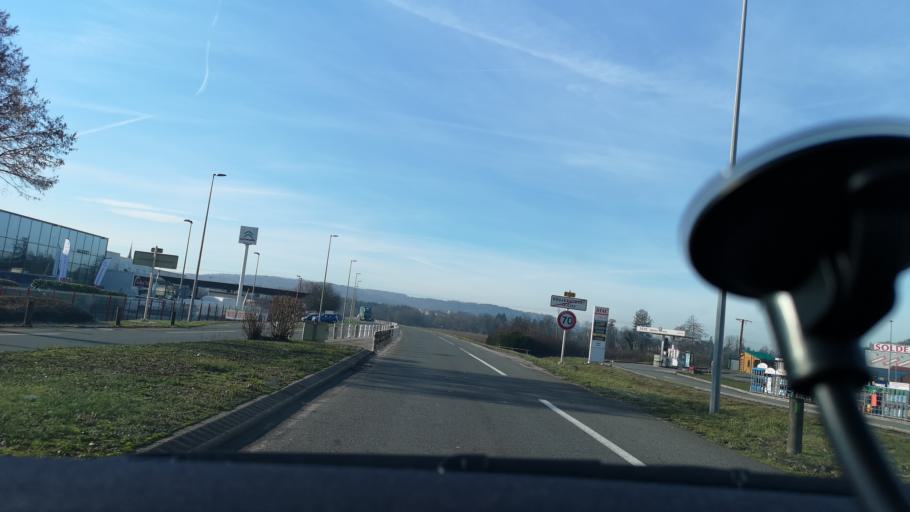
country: FR
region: Franche-Comte
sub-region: Departement du Doubs
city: Voujeaucourt
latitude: 47.4808
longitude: 6.7788
